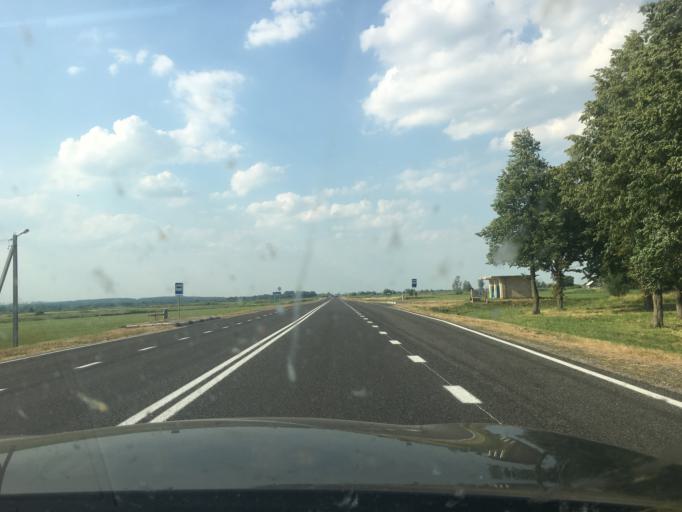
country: BY
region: Grodnenskaya
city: Indura
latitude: 53.3909
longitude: 23.9515
